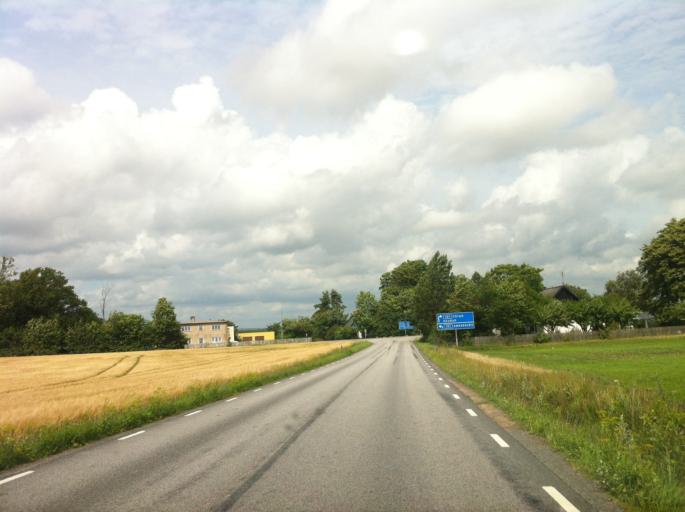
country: SE
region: Skane
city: Smygehamn
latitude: 55.3898
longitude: 13.4536
